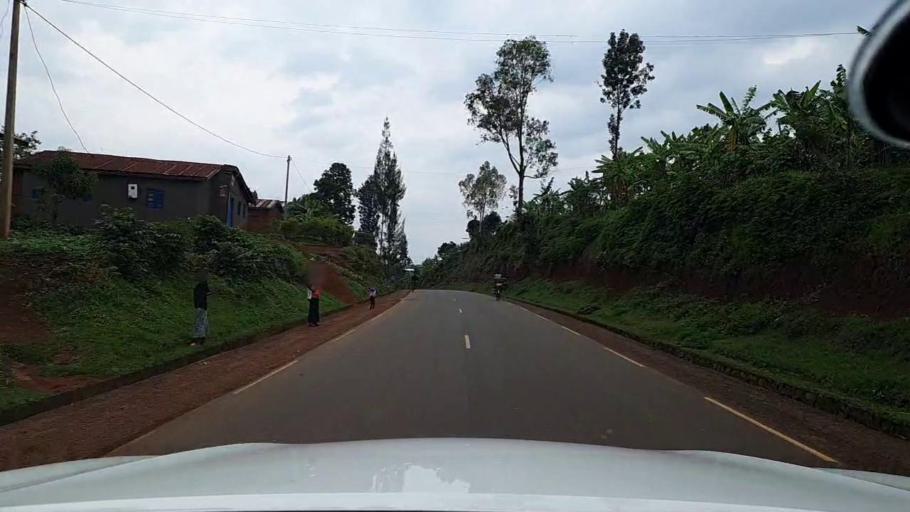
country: RW
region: Western Province
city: Cyangugu
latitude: -2.6093
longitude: 28.9356
